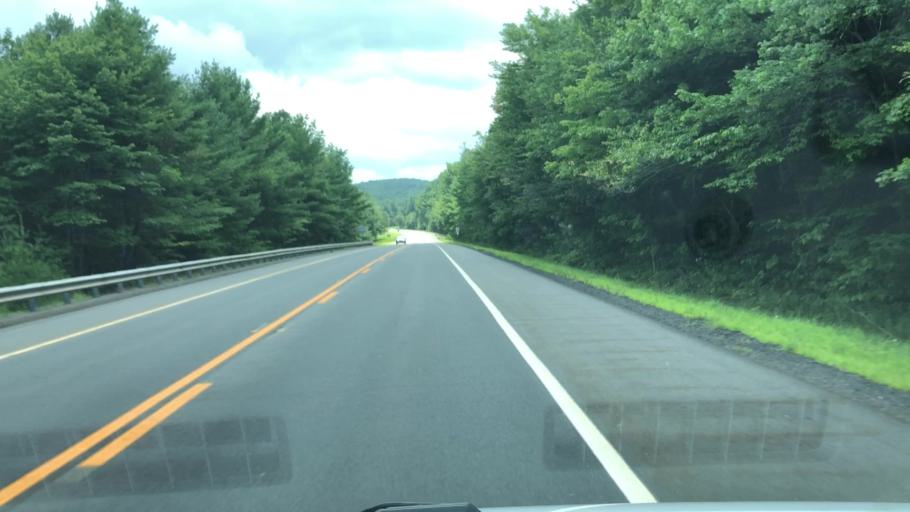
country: US
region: Massachusetts
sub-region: Franklin County
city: Ashfield
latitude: 42.4744
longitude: -72.8101
